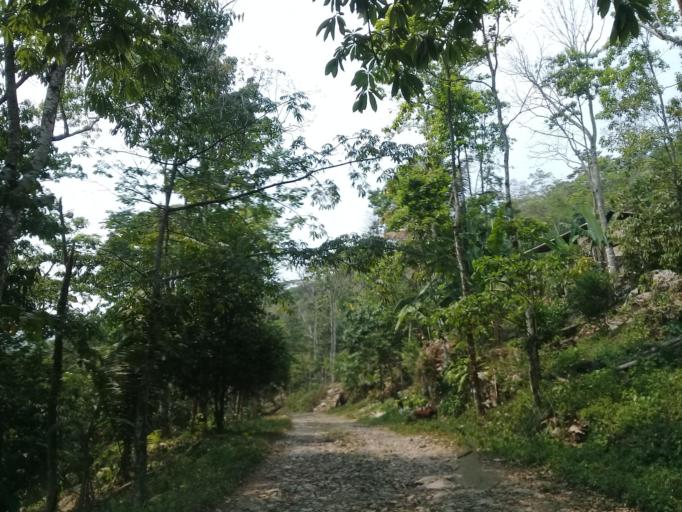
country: MX
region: Veracruz
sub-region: Tezonapa
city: Laguna Chica (Pueblo Nuevo)
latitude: 18.5818
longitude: -96.7553
